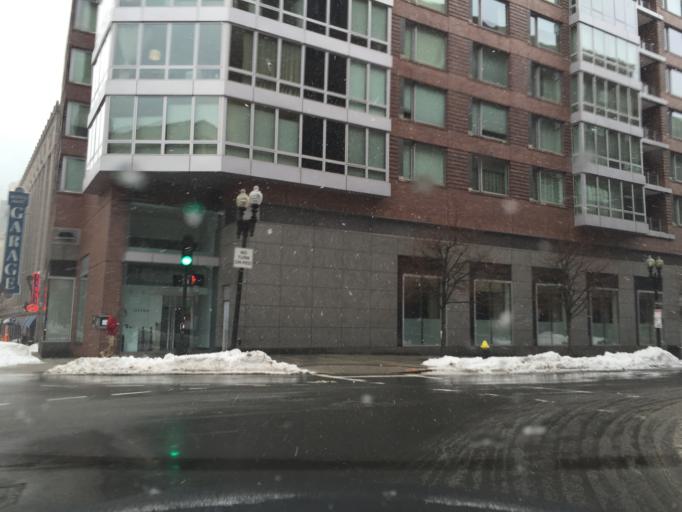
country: US
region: Massachusetts
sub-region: Suffolk County
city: Boston
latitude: 42.3508
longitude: -71.0667
